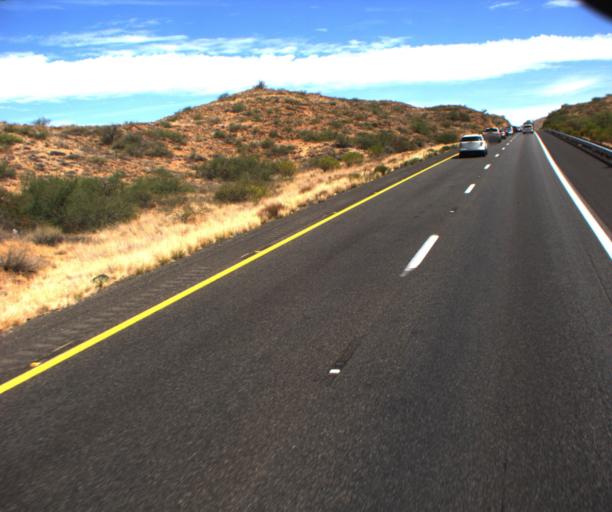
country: US
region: Arizona
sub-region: Yavapai County
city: Cordes Lakes
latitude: 34.2554
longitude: -112.1122
